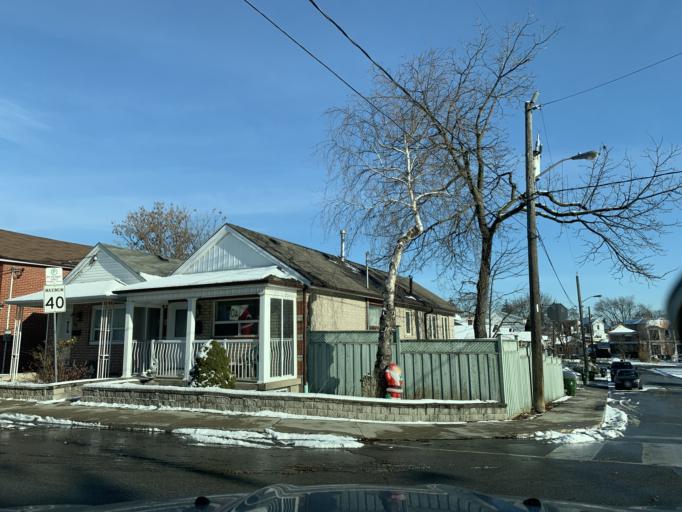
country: CA
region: Ontario
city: Toronto
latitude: 43.6769
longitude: -79.4783
